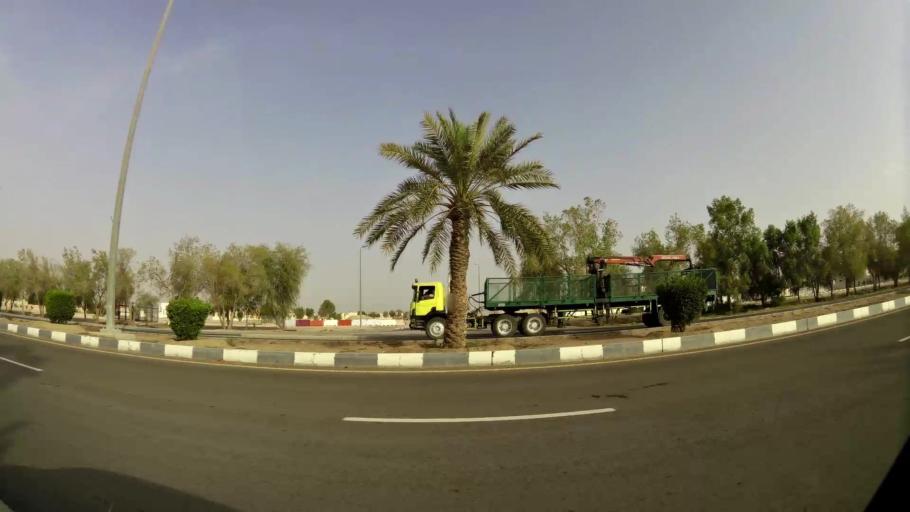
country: AE
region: Abu Dhabi
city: Al Ain
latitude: 24.1140
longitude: 55.7010
